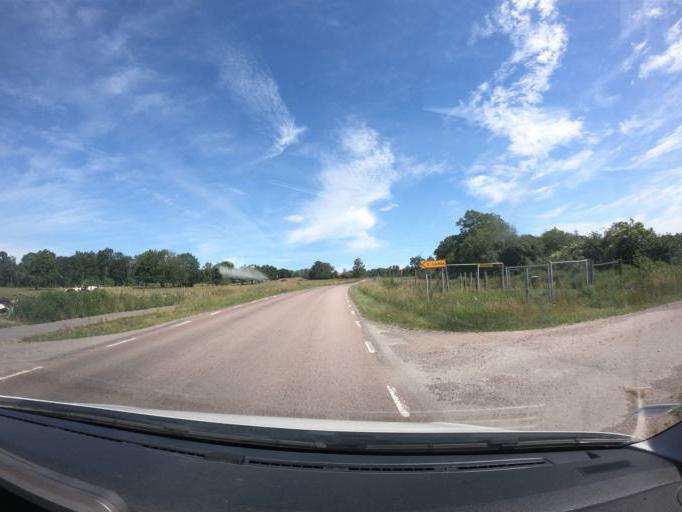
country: SE
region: Skane
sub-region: Klippans Kommun
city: Klippan
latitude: 56.1601
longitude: 13.1061
